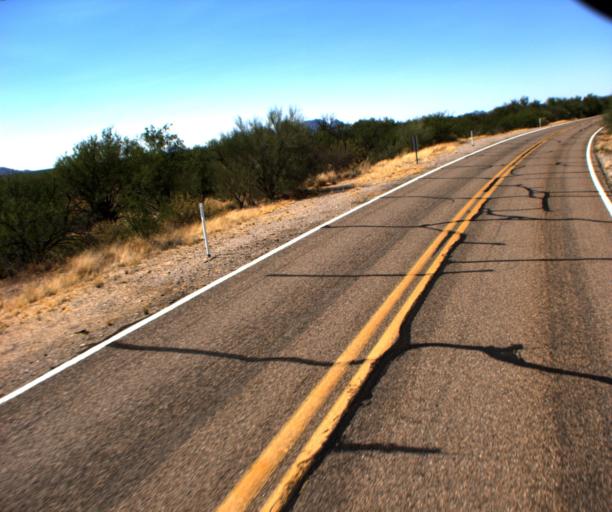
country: US
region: Arizona
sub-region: Pima County
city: Three Points
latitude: 31.9416
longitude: -111.3910
